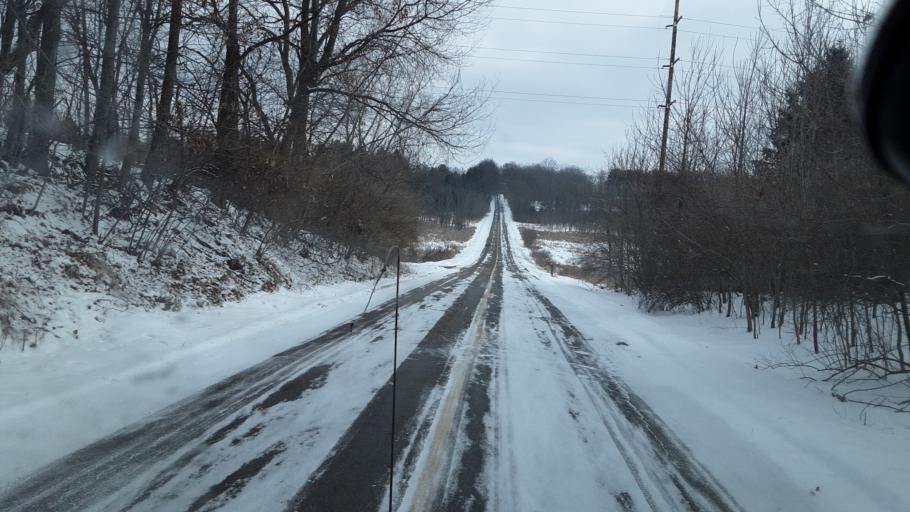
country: US
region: Michigan
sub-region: Ingham County
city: Leslie
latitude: 42.5020
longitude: -84.3749
